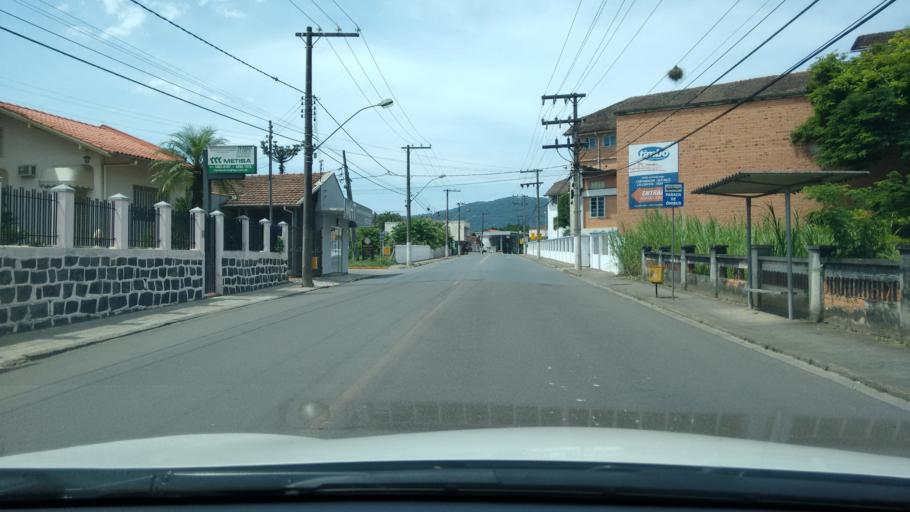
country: BR
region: Santa Catarina
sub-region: Timbo
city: Timbo
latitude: -26.8288
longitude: -49.2779
